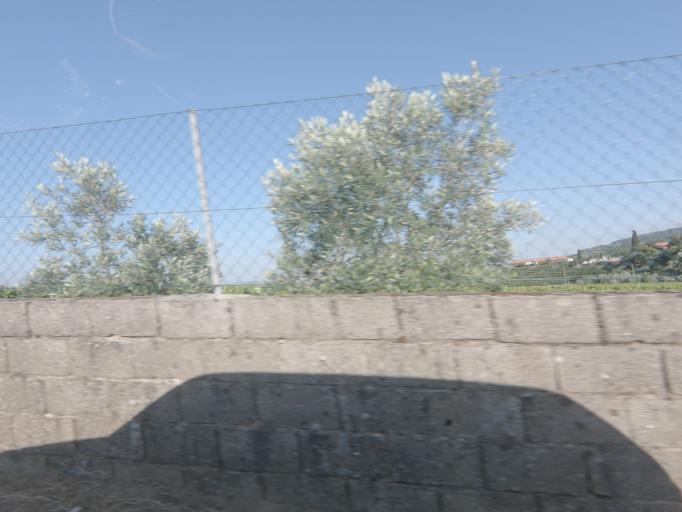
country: PT
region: Vila Real
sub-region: Sabrosa
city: Sabrosa
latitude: 41.2586
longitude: -7.5956
